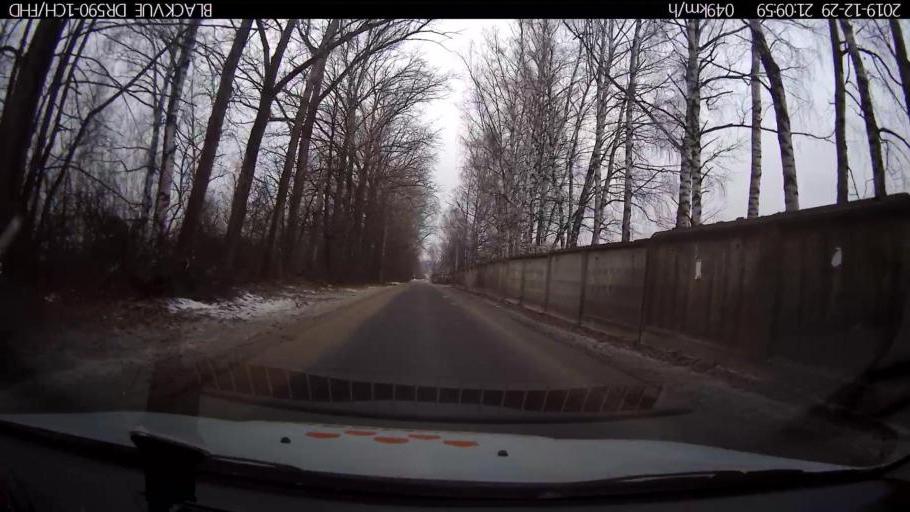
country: RU
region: Nizjnij Novgorod
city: Afonino
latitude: 56.2196
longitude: 44.0371
